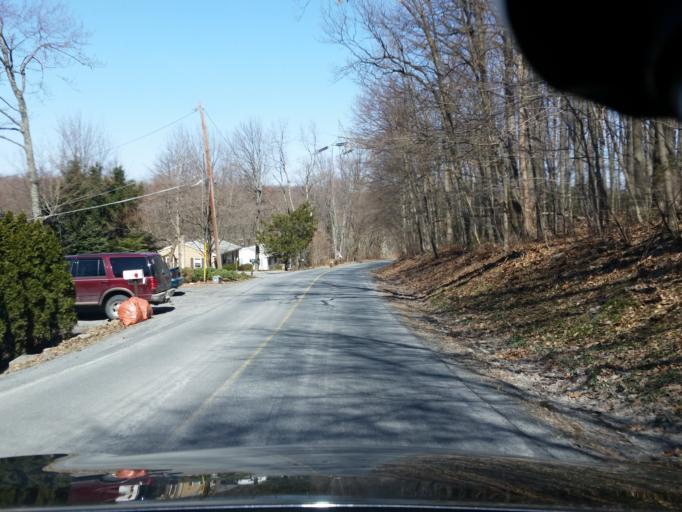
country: US
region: Pennsylvania
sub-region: Cumberland County
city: Schlusser
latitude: 40.2978
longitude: -77.1319
